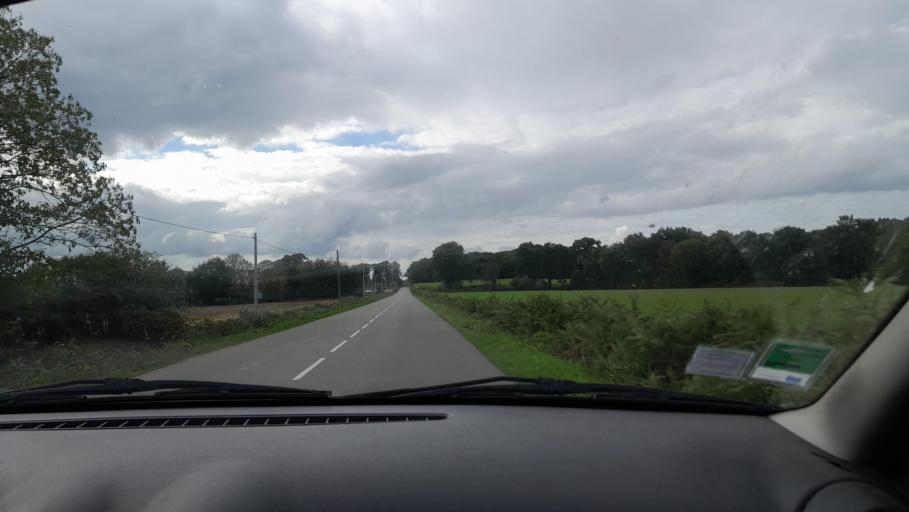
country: FR
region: Brittany
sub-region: Departement d'Ille-et-Vilaine
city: Le Pertre
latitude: 48.0428
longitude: -1.0645
